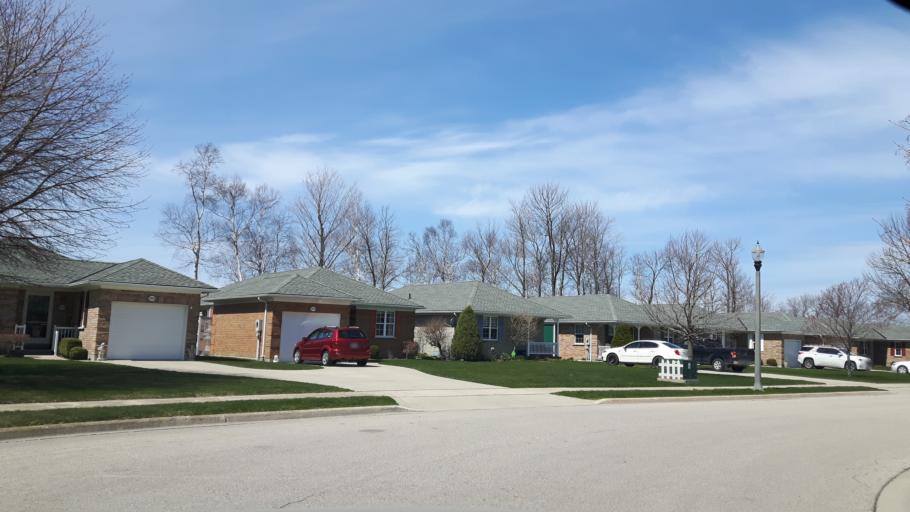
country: CA
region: Ontario
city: Goderich
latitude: 43.7285
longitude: -81.7231
